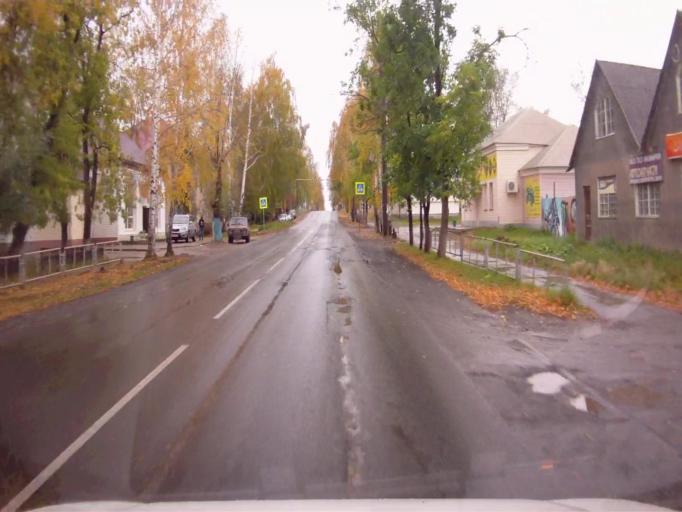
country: RU
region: Chelyabinsk
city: Verkhniy Ufaley
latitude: 56.0354
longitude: 60.2599
